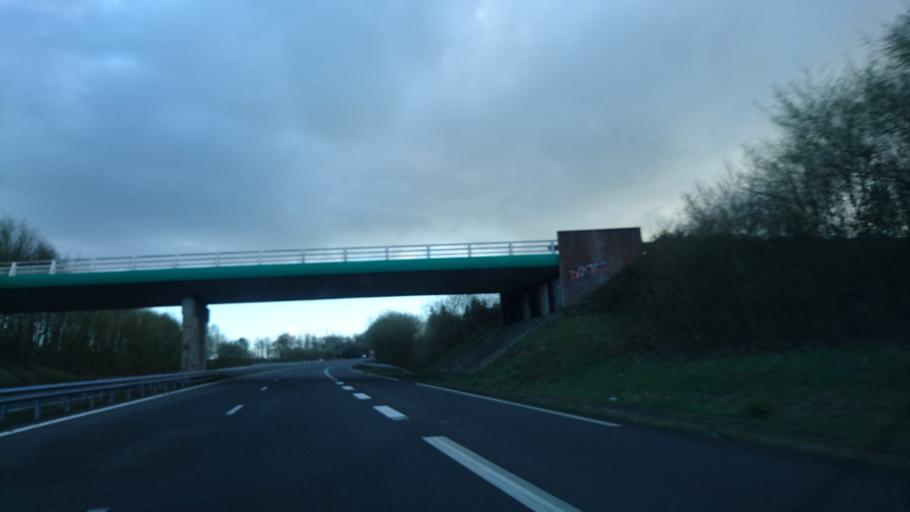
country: FR
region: Brittany
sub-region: Departement d'Ille-et-Vilaine
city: Chasne-sur-Illet
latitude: 48.2778
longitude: -1.6002
